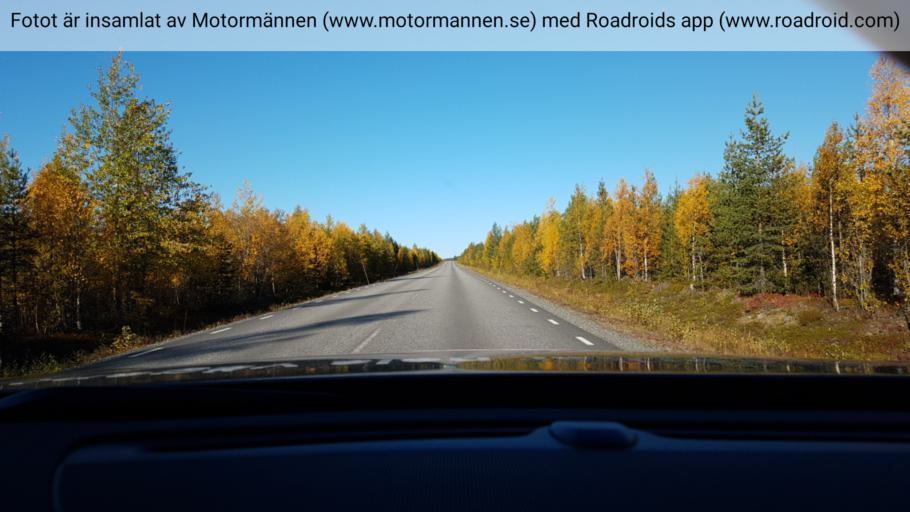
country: SE
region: Vaesterbotten
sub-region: Skelleftea Kommun
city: Storvik
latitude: 65.3256
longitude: 20.6919
